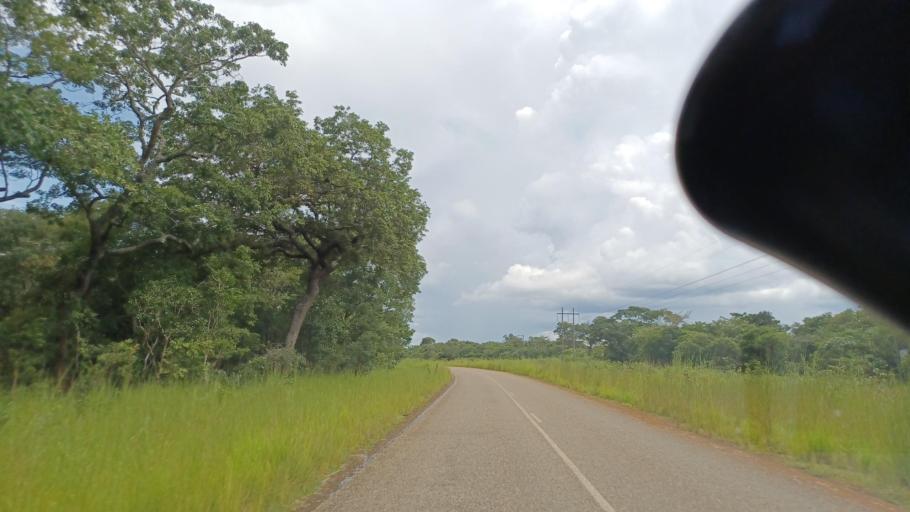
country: ZM
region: North-Western
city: Kasempa
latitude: -13.1522
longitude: 25.8775
